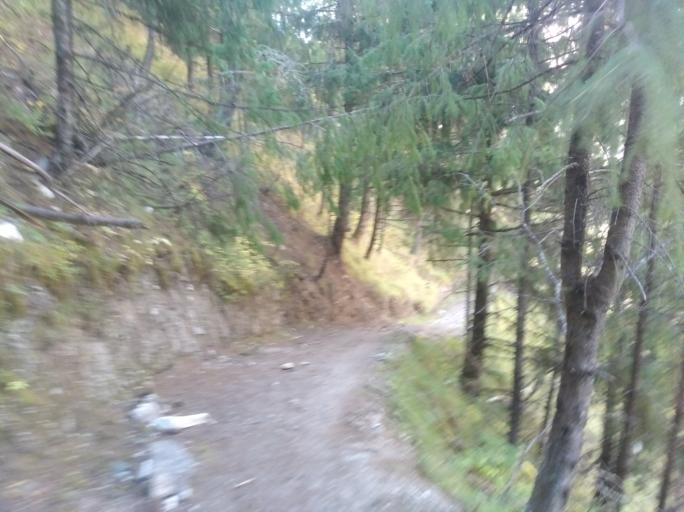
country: NP
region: Western Region
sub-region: Dhawalagiri Zone
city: Jomsom
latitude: 28.8916
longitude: 83.0468
